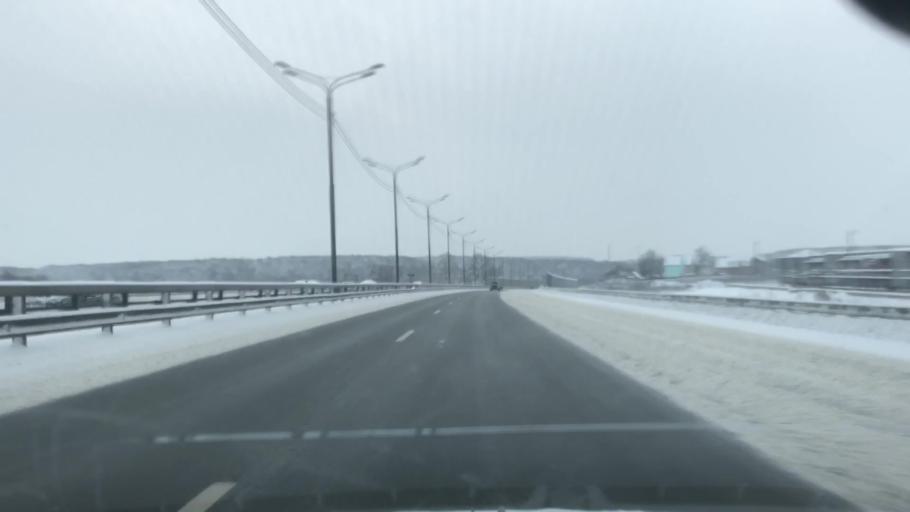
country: RU
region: Moskovskaya
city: Barybino
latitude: 55.2830
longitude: 37.8602
